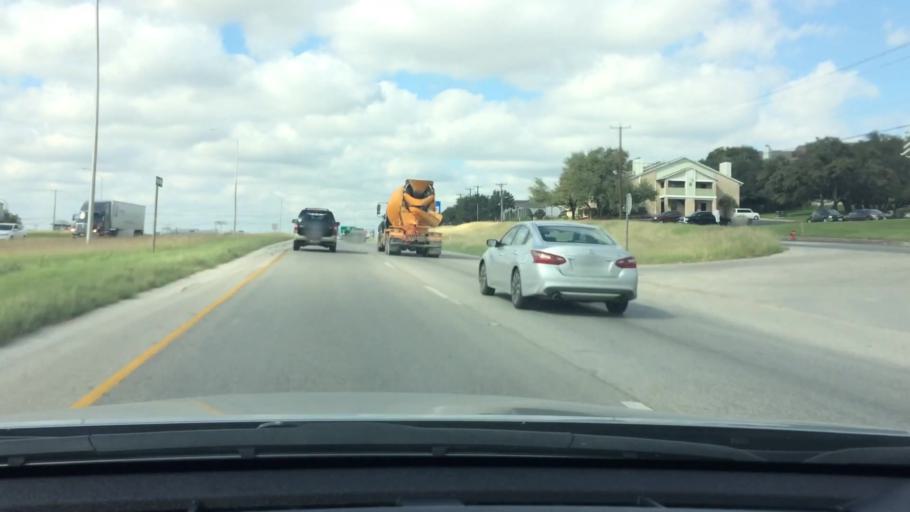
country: US
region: Texas
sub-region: Bexar County
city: Live Oak
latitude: 29.5541
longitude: -98.3227
